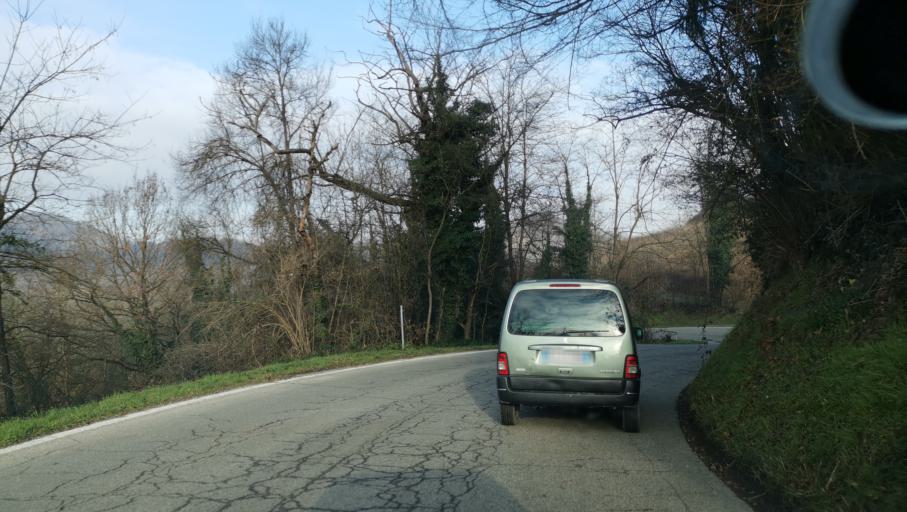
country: IT
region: Piedmont
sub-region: Provincia di Asti
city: Berzano di San Pietro
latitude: 45.1010
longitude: 7.9414
